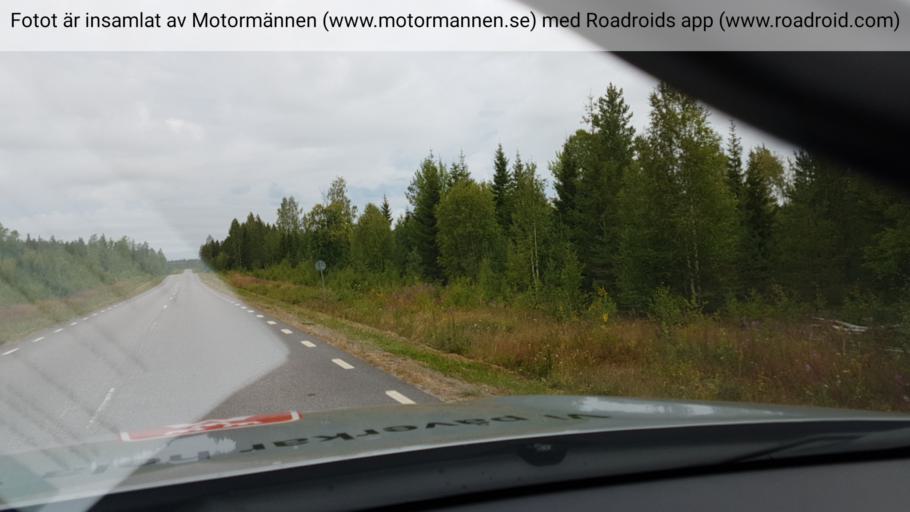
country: SE
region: Norrbotten
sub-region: Bodens Kommun
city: Saevast
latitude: 65.6666
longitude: 21.6617
